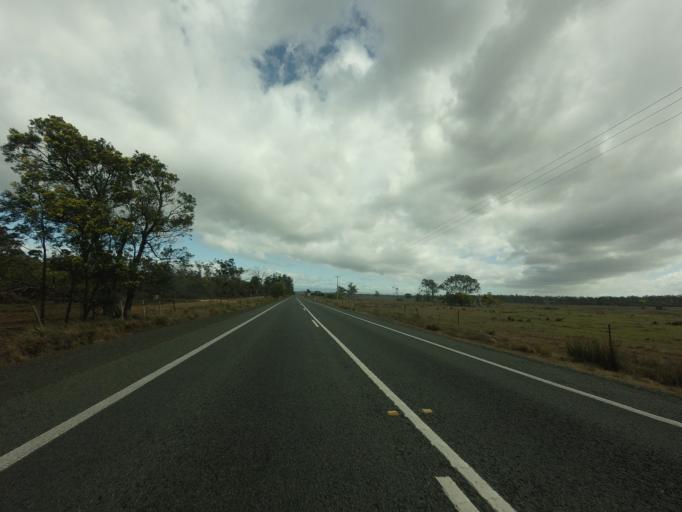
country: AU
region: Tasmania
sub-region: Northern Midlands
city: Evandale
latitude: -41.8312
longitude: 147.4835
